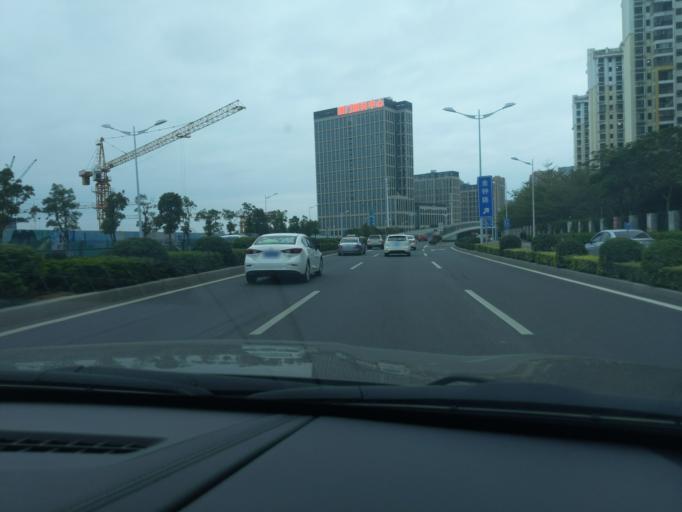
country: CN
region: Fujian
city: Liuwudian
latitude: 24.5100
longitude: 118.1838
